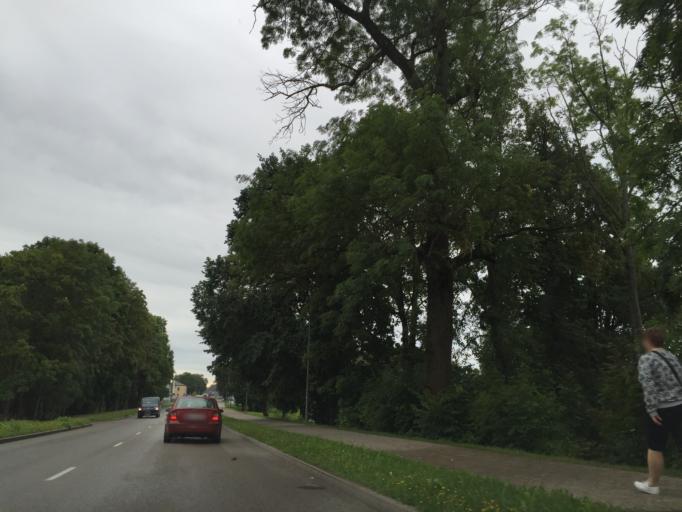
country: LV
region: Jekabpils Rajons
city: Jekabpils
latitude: 56.5088
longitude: 25.8608
